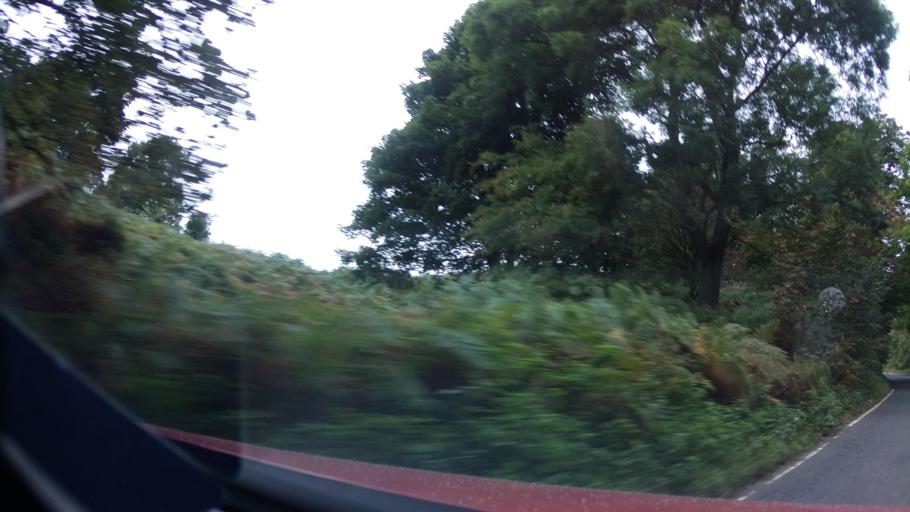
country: GB
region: Scotland
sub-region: Fife
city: Kinglassie
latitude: 56.1980
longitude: -3.2653
